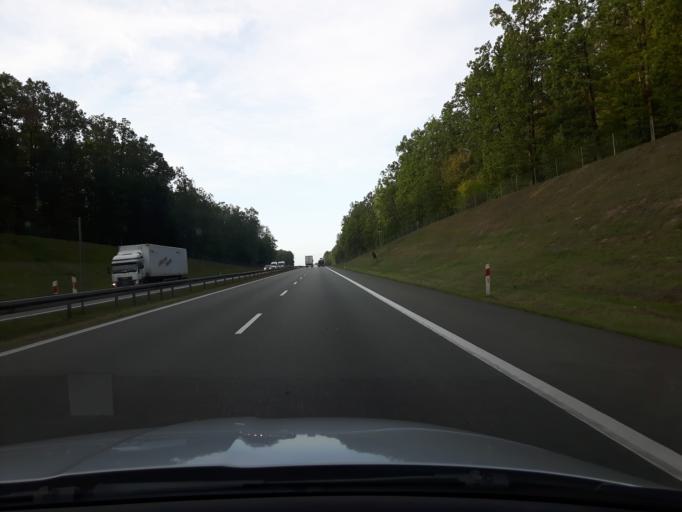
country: PL
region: Masovian Voivodeship
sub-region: Powiat bialobrzeski
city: Bialobrzegi
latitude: 51.6402
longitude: 20.9726
